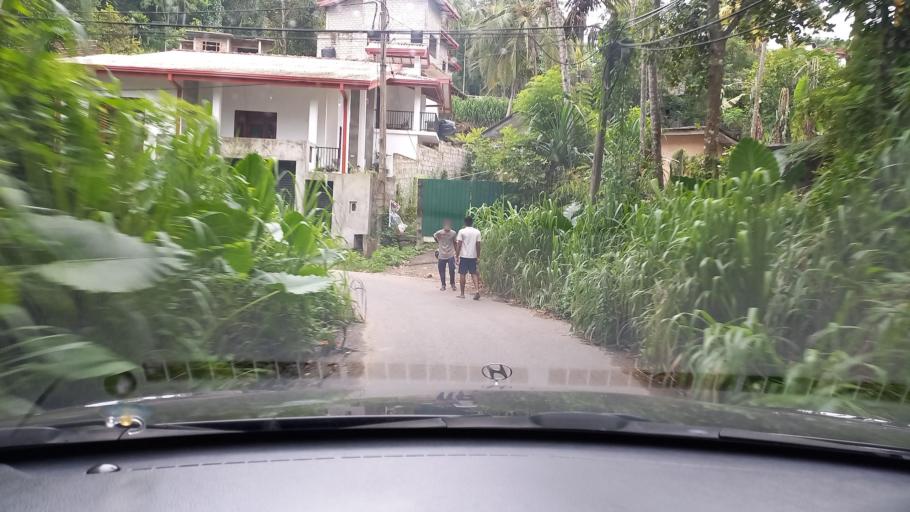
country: LK
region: Central
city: Kadugannawa
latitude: 7.2599
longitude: 80.3552
